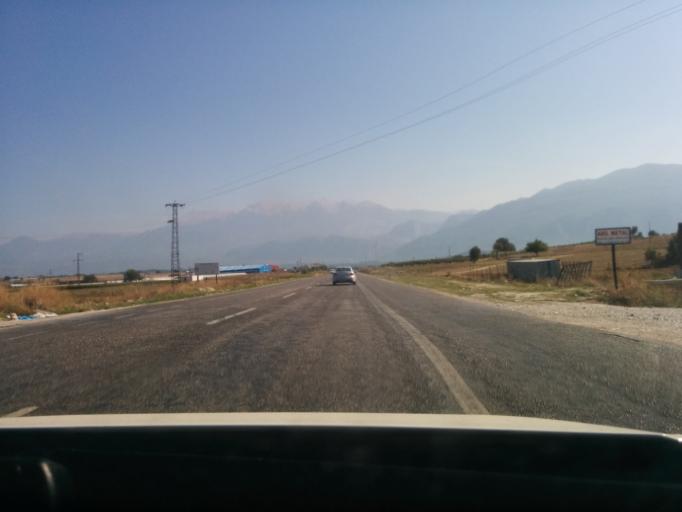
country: TR
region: Mugla
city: Esen
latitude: 36.4418
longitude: 29.2789
